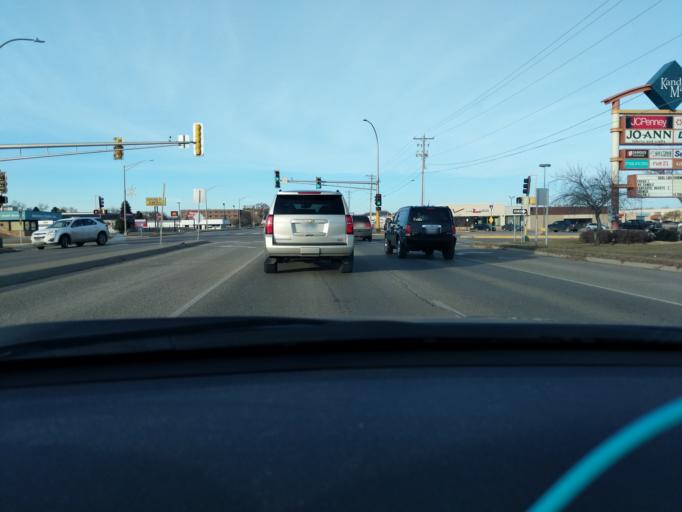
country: US
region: Minnesota
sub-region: Kandiyohi County
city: Willmar
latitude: 45.1053
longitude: -95.0426
